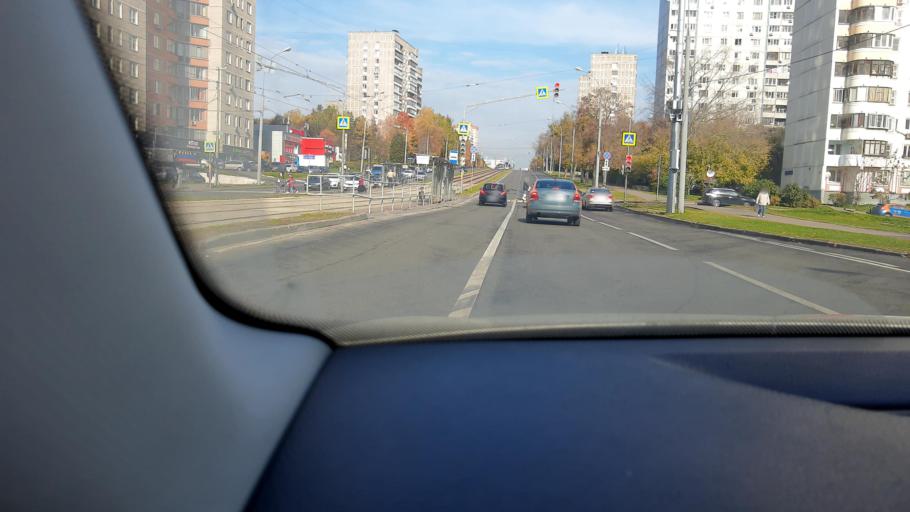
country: RU
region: Moscow
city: Chertanovo Yuzhnoye
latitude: 55.6056
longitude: 37.5912
